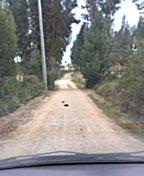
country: CO
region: Boyaca
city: Paipa
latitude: 5.8213
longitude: -73.0877
